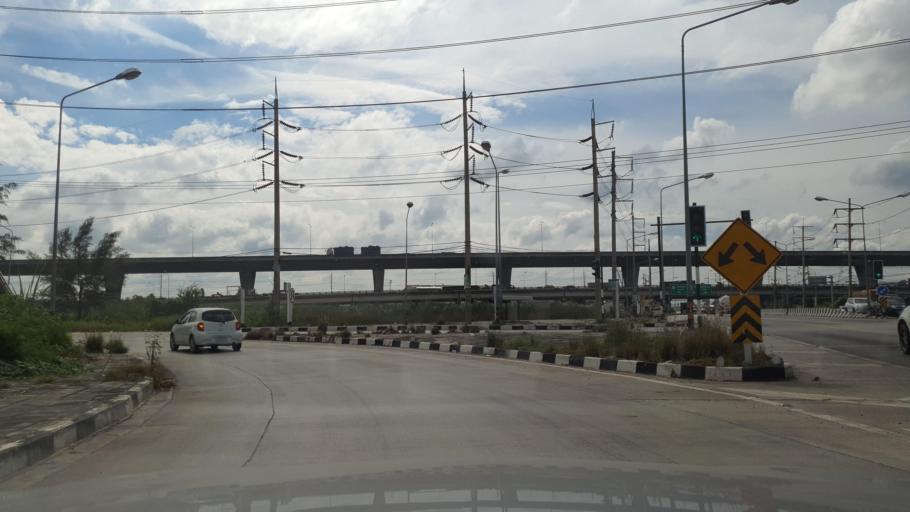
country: TH
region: Chachoengsao
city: Bang Pakong
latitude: 13.5131
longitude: 100.9880
